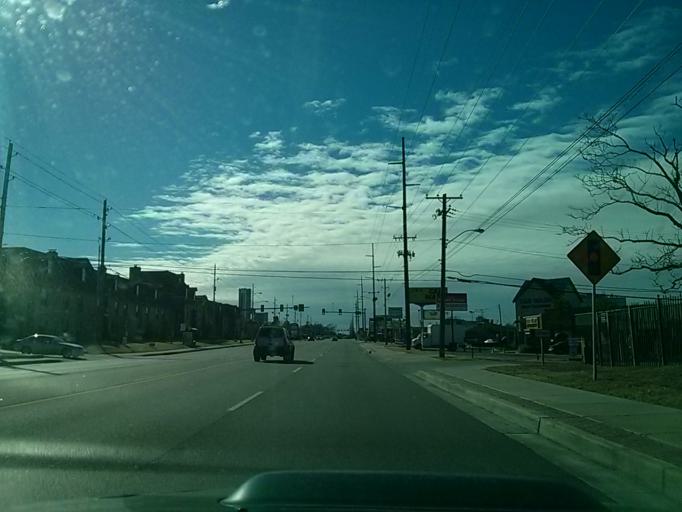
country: US
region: Oklahoma
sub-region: Tulsa County
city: Jenks
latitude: 36.0649
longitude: -95.9580
